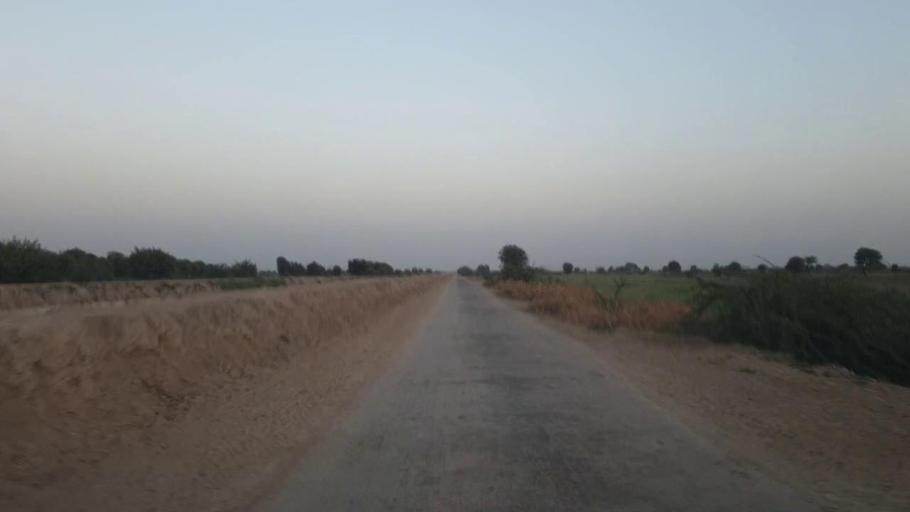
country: PK
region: Sindh
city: Umarkot
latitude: 25.4161
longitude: 69.6733
